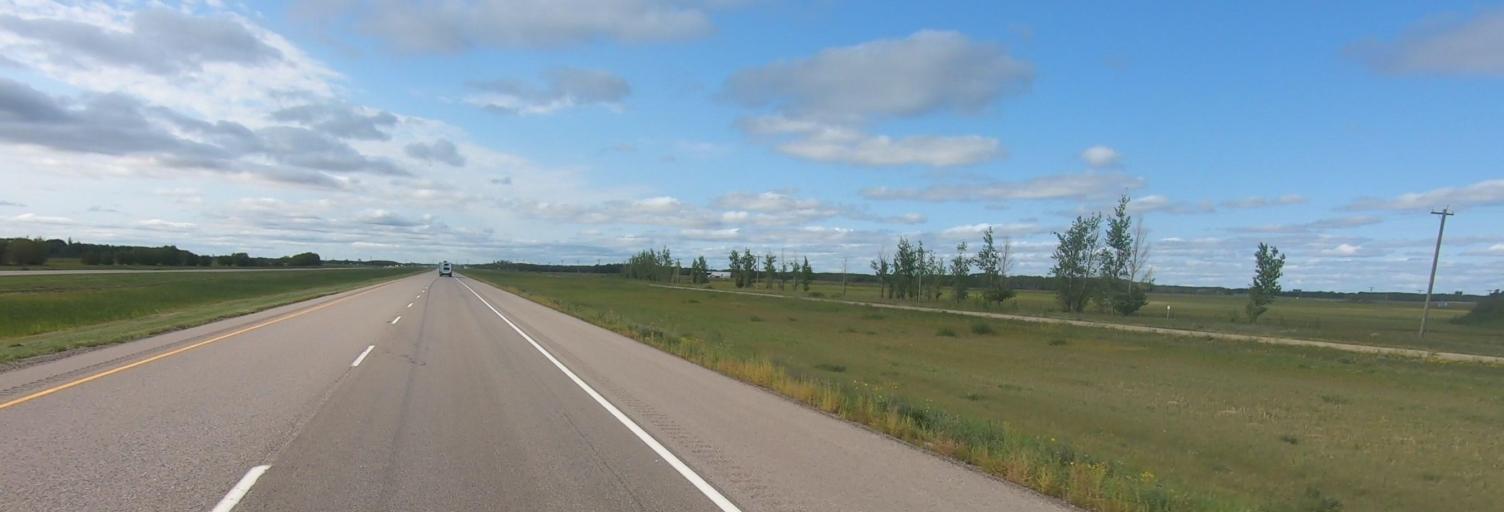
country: CA
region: Manitoba
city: Virden
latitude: 49.8176
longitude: -100.8610
